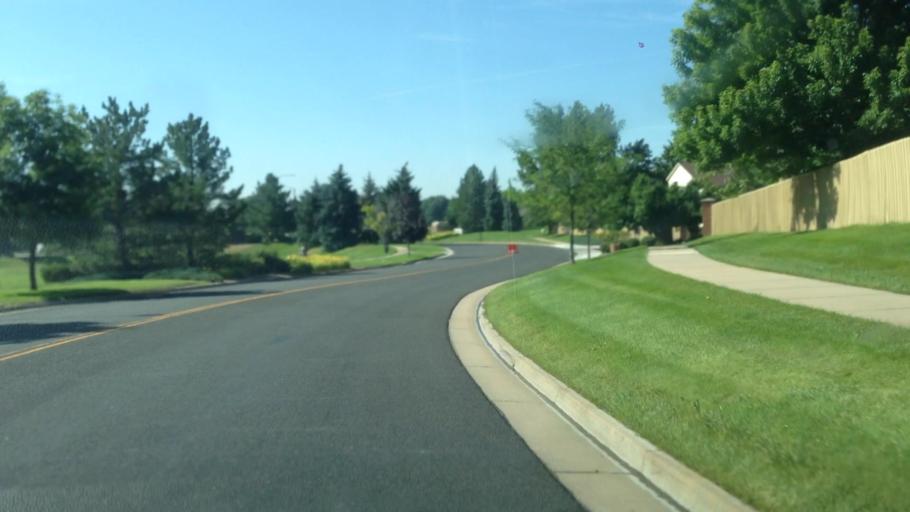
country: US
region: Colorado
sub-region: Douglas County
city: Stonegate
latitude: 39.5191
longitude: -104.7867
